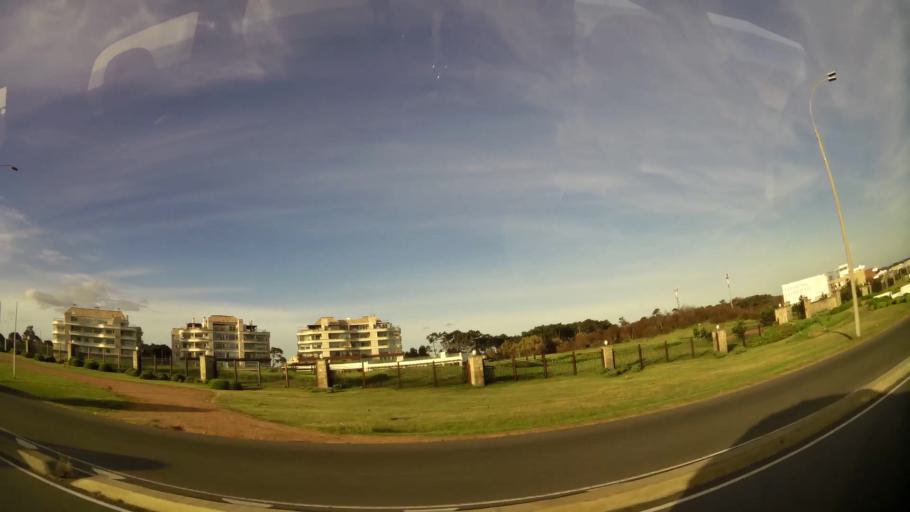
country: UY
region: Maldonado
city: Maldonado
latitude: -34.9091
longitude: -55.0177
